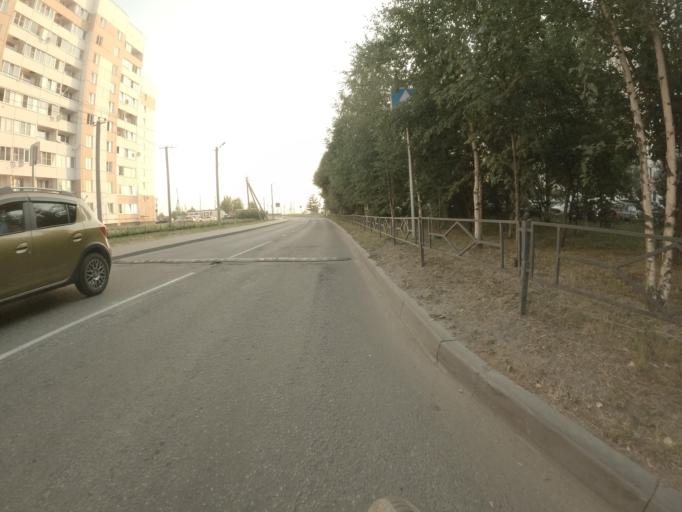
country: RU
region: St.-Petersburg
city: Pontonnyy
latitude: 59.7995
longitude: 30.6374
